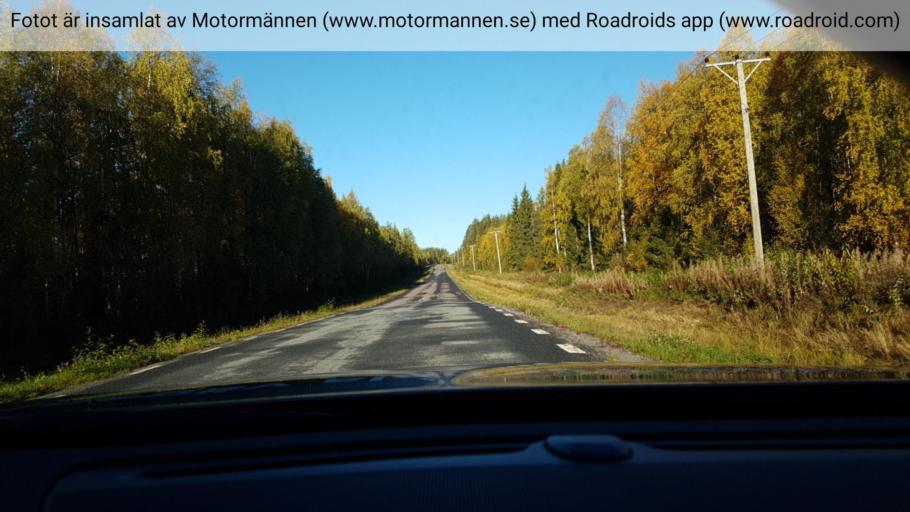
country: SE
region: Norrbotten
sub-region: Bodens Kommun
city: Boden
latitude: 65.9493
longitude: 21.6211
